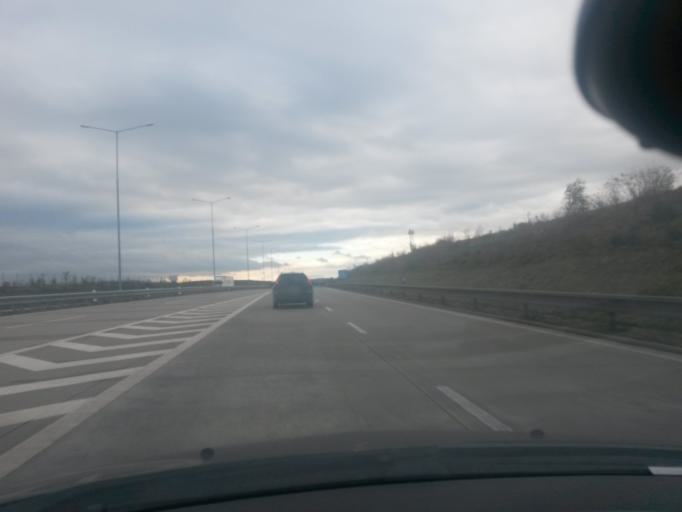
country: CZ
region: Central Bohemia
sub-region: Okres Praha-Zapad
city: Pruhonice
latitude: 49.9772
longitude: 14.5930
